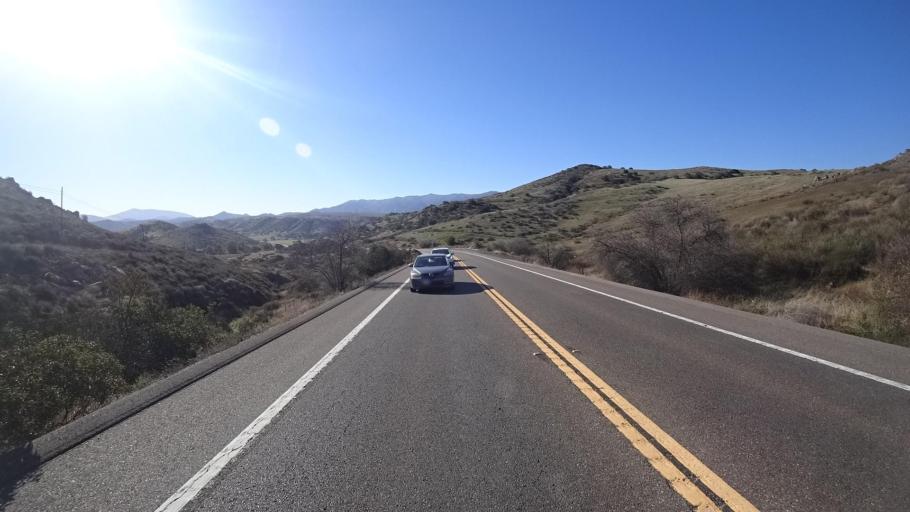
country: US
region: California
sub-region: San Diego County
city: Jamul
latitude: 32.6801
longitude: -116.8403
